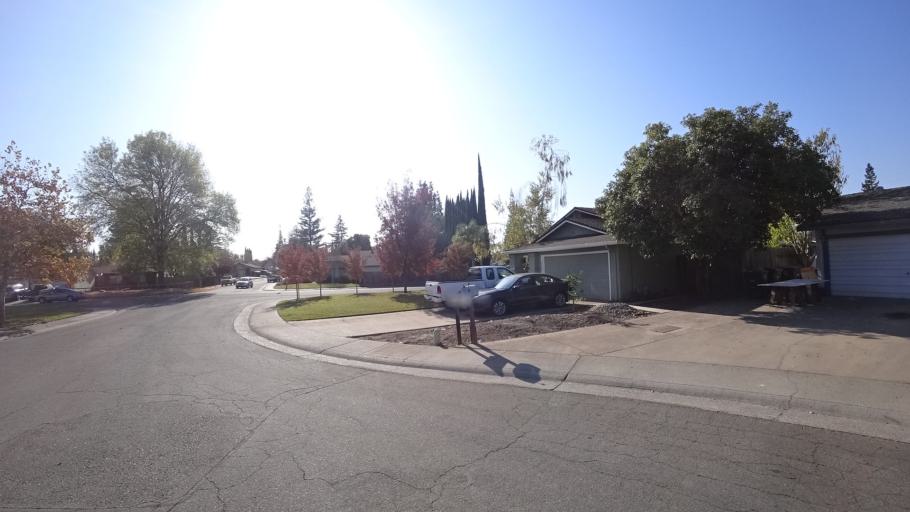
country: US
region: California
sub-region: Sacramento County
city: Citrus Heights
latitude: 38.6976
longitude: -121.2516
